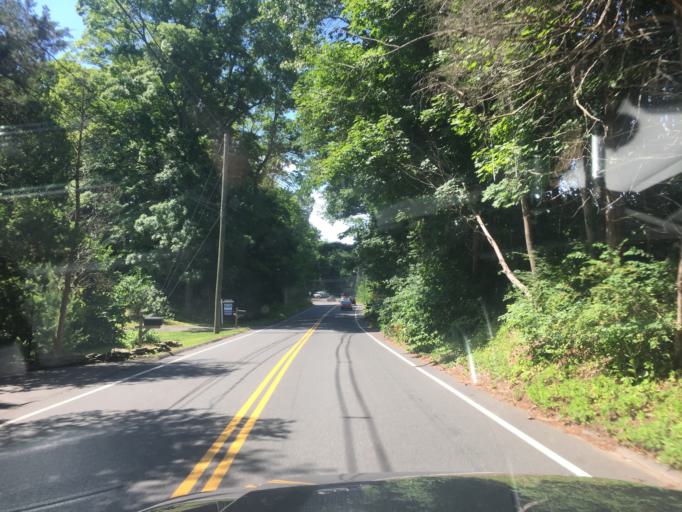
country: US
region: Connecticut
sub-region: Hartford County
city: Farmington
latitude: 41.7614
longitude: -72.8180
